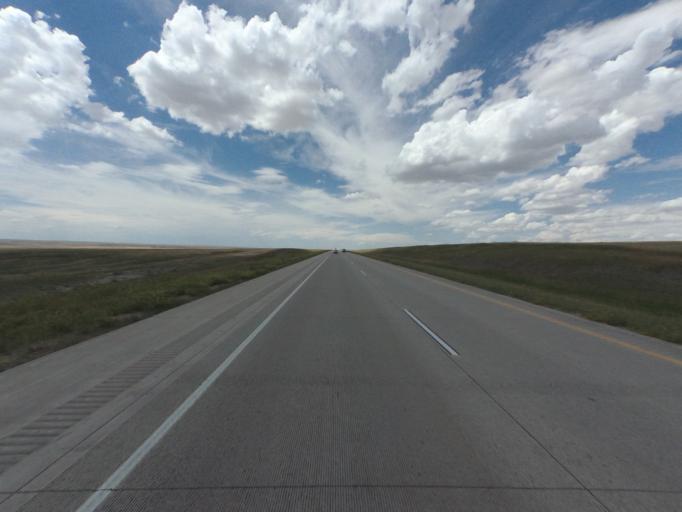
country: US
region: Colorado
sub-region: Lincoln County
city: Limon
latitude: 39.3893
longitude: -103.8932
